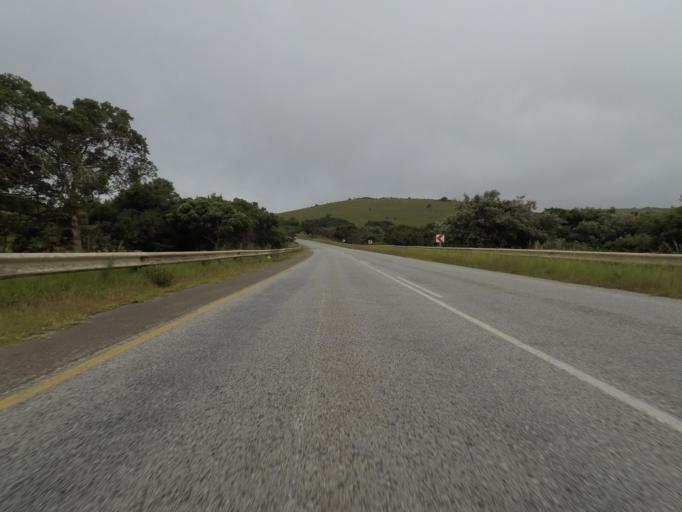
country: ZA
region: Eastern Cape
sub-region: Cacadu District Municipality
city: Port Alfred
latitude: -33.6142
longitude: 26.8022
